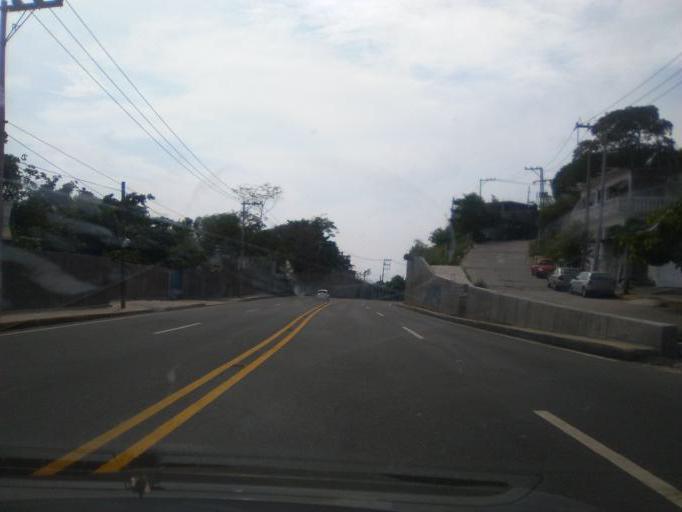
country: MX
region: Guerrero
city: Acapulco de Juarez
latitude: 16.8840
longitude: -99.9533
